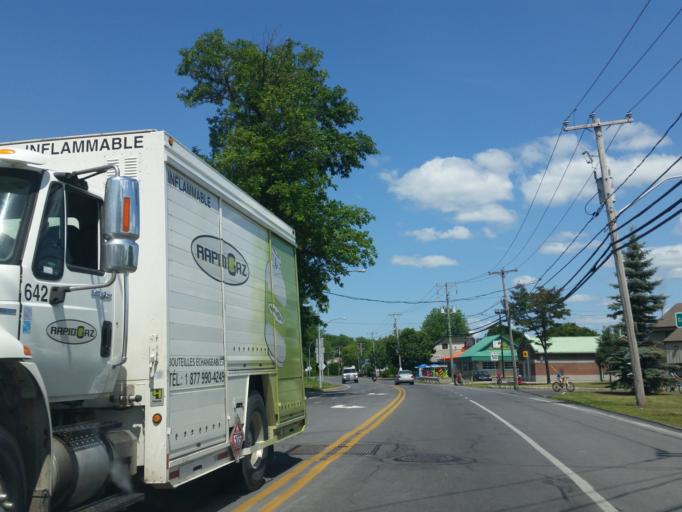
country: CA
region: Quebec
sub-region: Monteregie
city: Saint-Jean-sur-Richelieu
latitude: 45.3484
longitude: -73.2654
